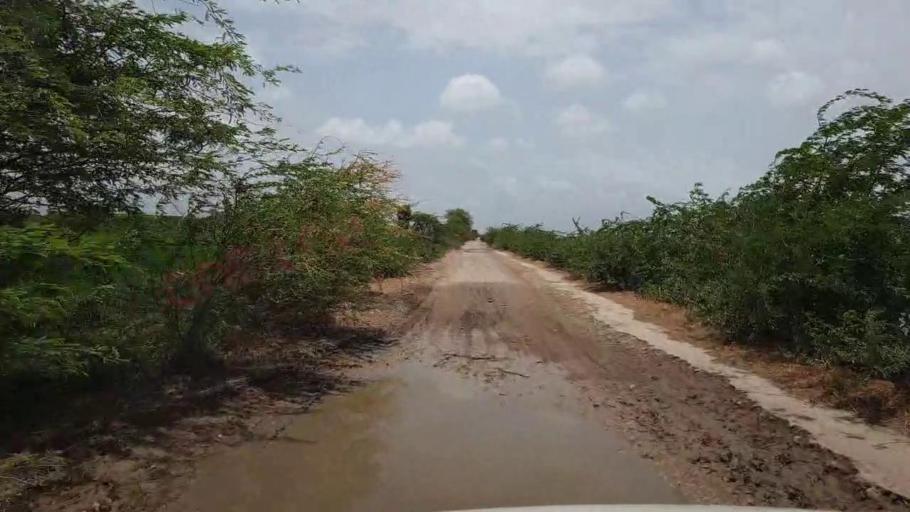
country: PK
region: Sindh
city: Kario
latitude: 24.7225
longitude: 68.5656
